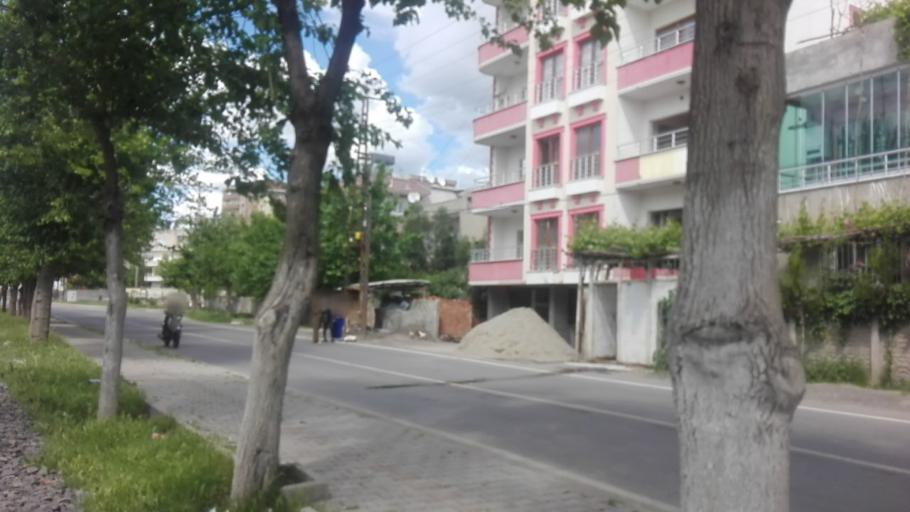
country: TR
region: Batman
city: Batman
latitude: 37.8943
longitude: 41.1461
